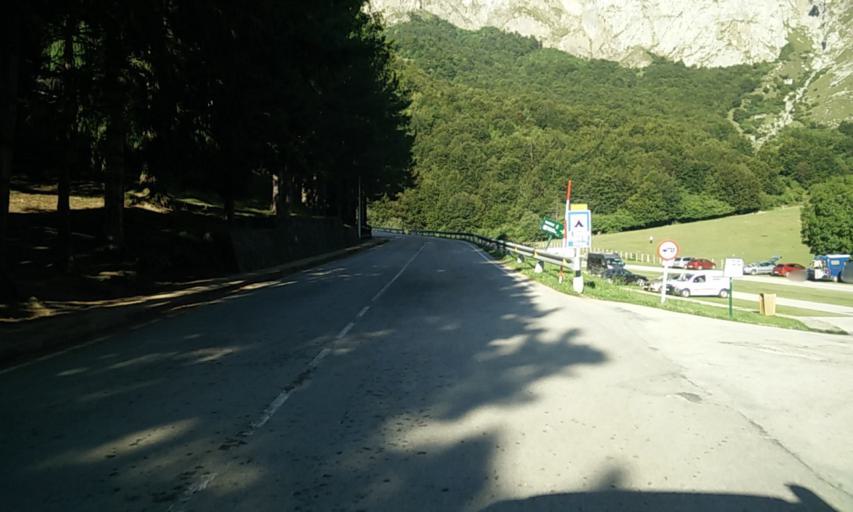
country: ES
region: Castille and Leon
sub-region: Provincia de Leon
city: Posada de Valdeon
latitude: 43.1443
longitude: -4.8115
